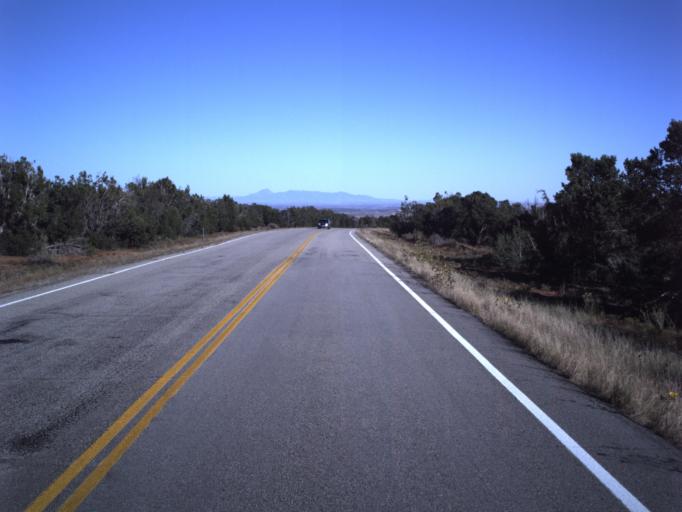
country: US
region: Utah
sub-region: San Juan County
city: Blanding
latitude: 37.5561
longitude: -109.7843
